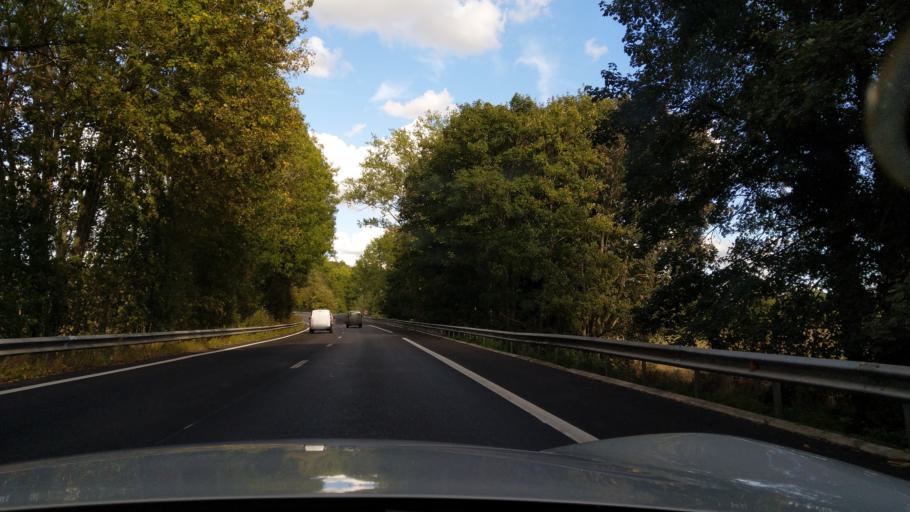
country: FR
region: Ile-de-France
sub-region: Departement de Seine-et-Marne
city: Bouleurs
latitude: 48.8824
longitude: 2.8913
